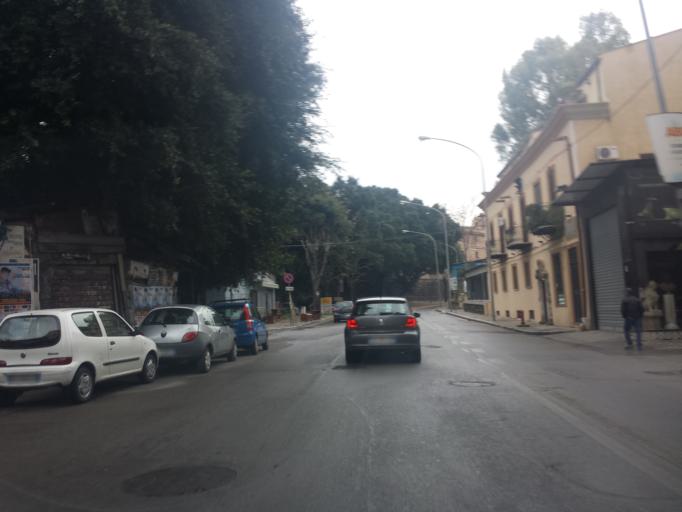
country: IT
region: Sicily
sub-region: Palermo
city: Palermo
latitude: 38.1148
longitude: 13.3518
